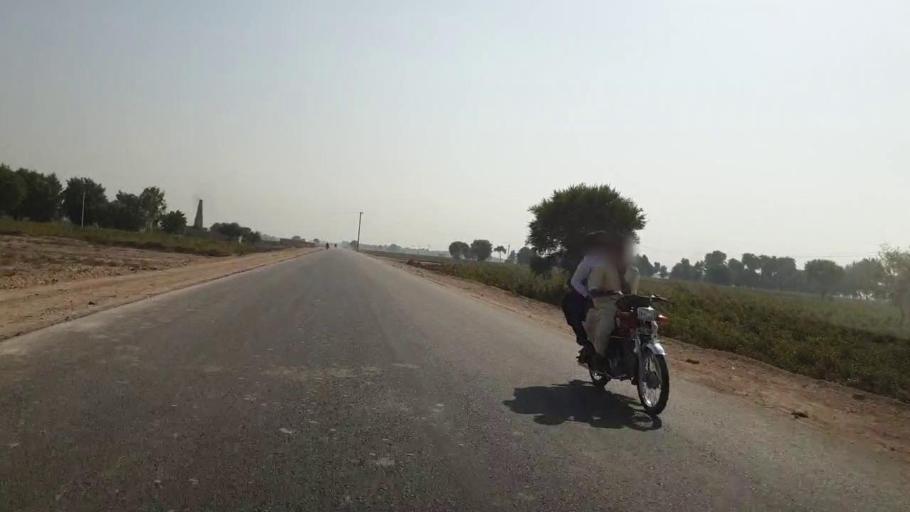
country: PK
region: Sindh
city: Dadu
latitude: 26.6626
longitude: 67.7764
